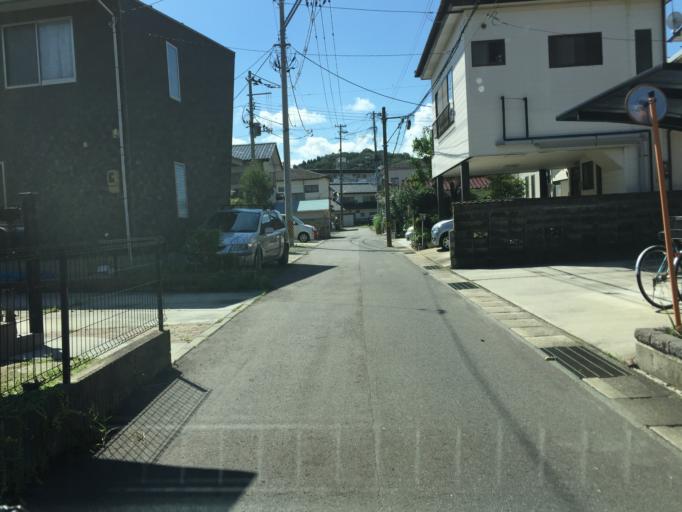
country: JP
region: Fukushima
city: Fukushima-shi
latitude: 37.7254
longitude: 140.4602
